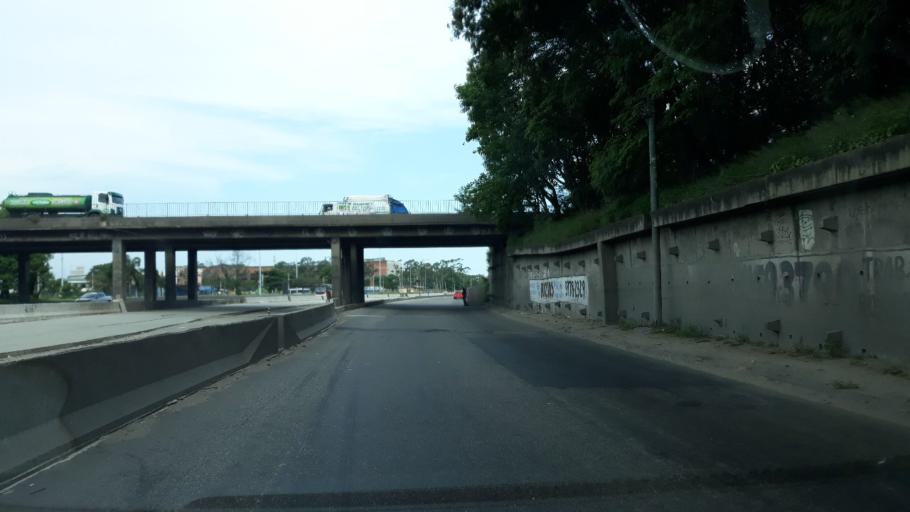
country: BR
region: Rio de Janeiro
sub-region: Duque De Caxias
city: Duque de Caxias
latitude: -22.8159
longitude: -43.2895
